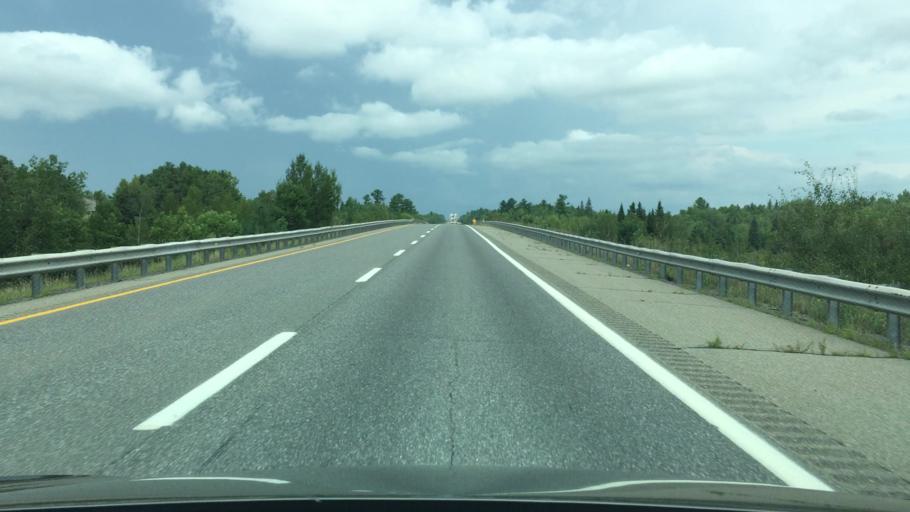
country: US
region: Maine
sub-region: Penobscot County
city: Lincoln
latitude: 45.3935
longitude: -68.6011
